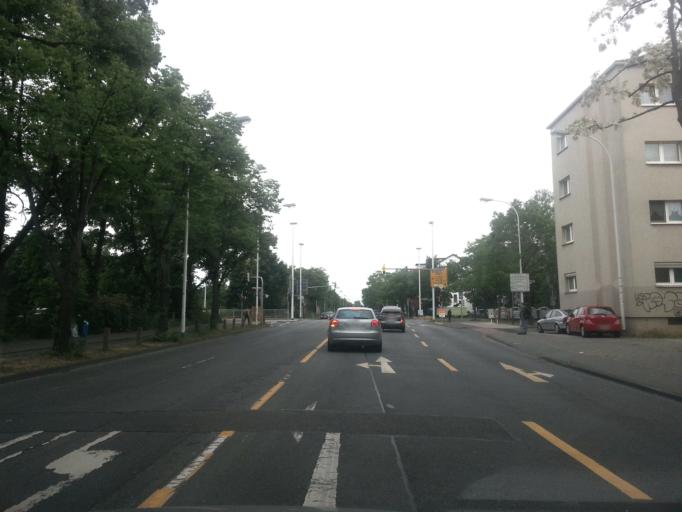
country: DE
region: Hesse
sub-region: Regierungsbezirk Darmstadt
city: Darmstadt
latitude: 49.8582
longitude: 8.6354
